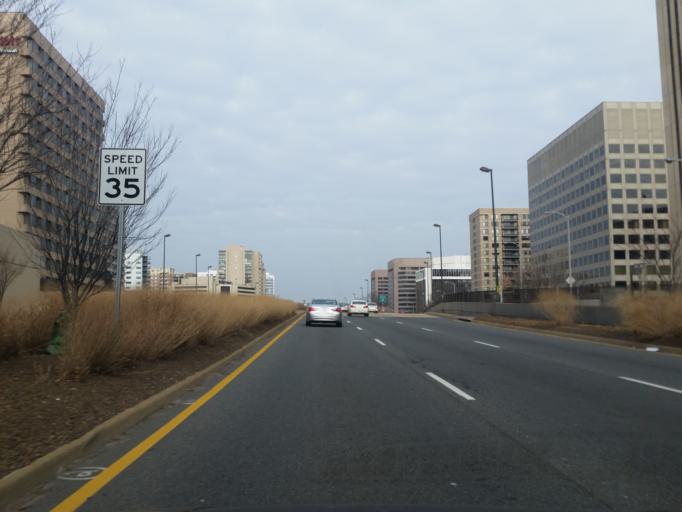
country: US
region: Washington, D.C.
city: Washington, D.C.
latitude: 38.8568
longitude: -77.0521
